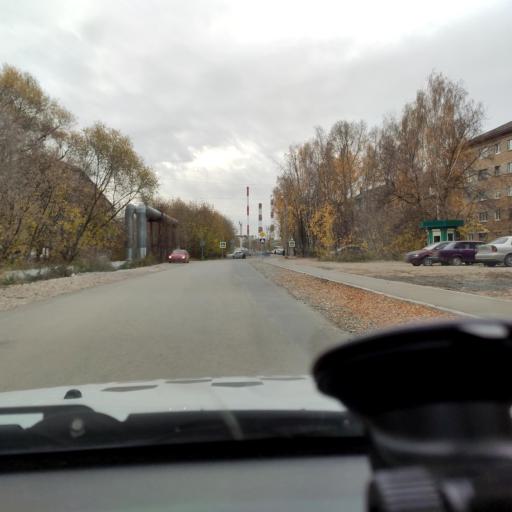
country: RU
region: Perm
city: Perm
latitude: 57.9880
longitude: 56.2610
